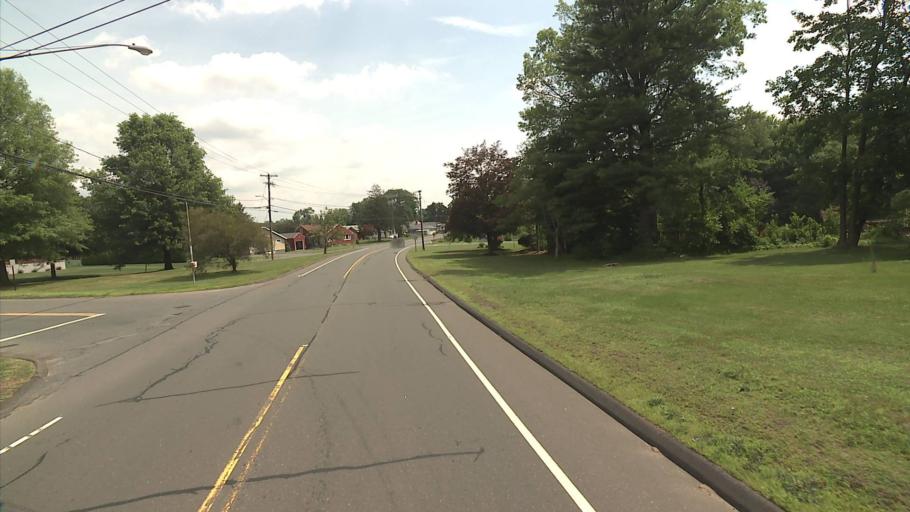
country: US
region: Connecticut
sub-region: Middlesex County
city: Middletown
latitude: 41.5324
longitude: -72.6496
